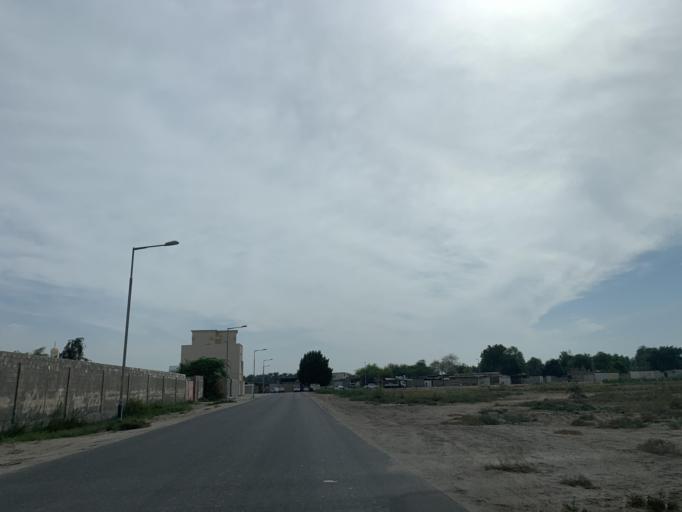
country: BH
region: Central Governorate
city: Madinat Hamad
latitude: 26.1179
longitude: 50.4749
